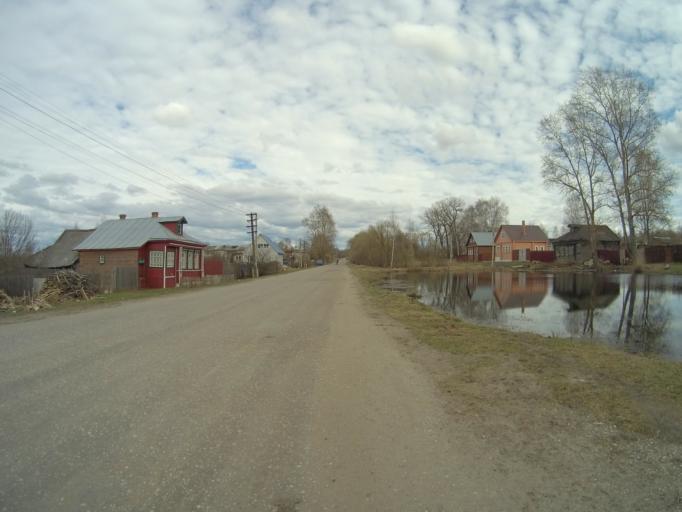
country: RU
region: Vladimir
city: Sudogda
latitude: 55.9761
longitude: 40.7282
